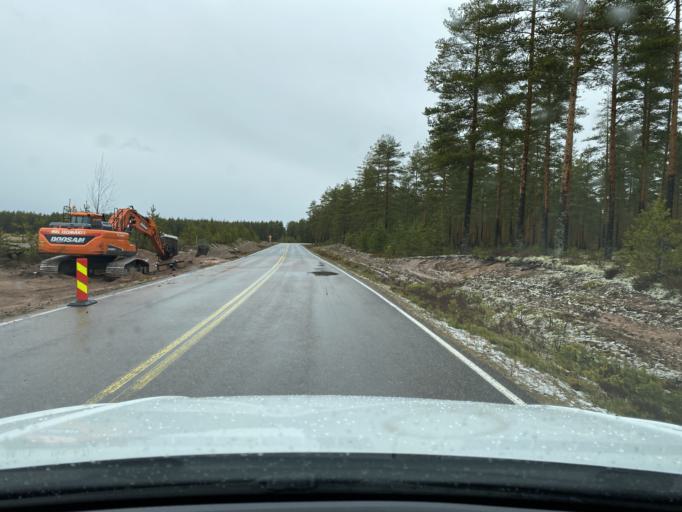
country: FI
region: Satakunta
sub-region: Pori
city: Vampula
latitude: 60.9623
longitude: 22.6766
